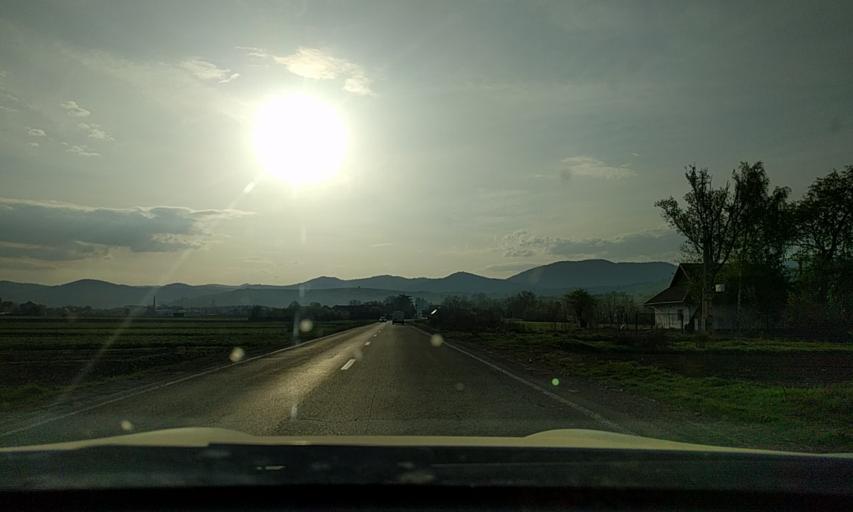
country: RO
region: Covasna
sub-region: Comuna Bretcu
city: Bretcu
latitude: 46.0421
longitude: 26.2851
